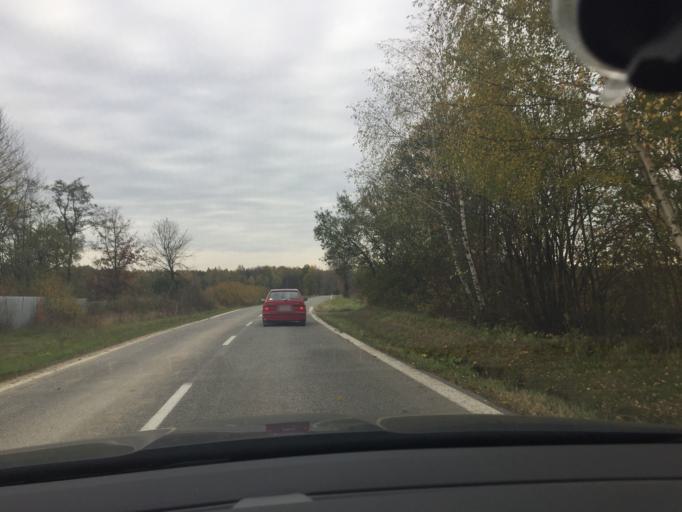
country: SK
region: Presovsky
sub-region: Okres Presov
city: Presov
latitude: 48.9418
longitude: 21.3033
